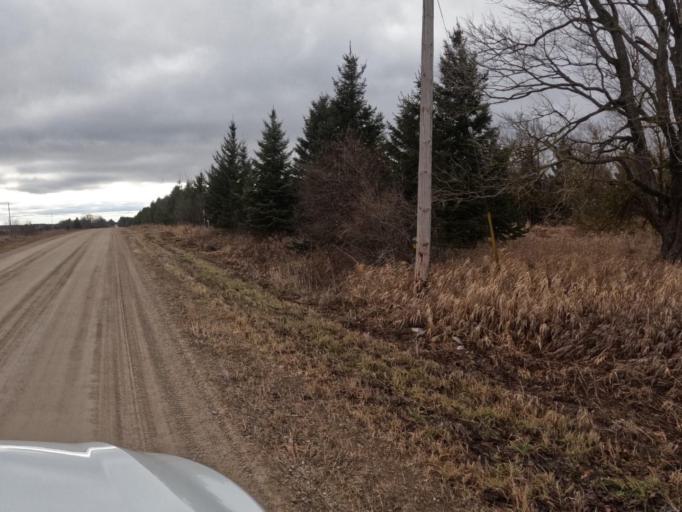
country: CA
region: Ontario
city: Shelburne
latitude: 43.9761
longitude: -80.4038
